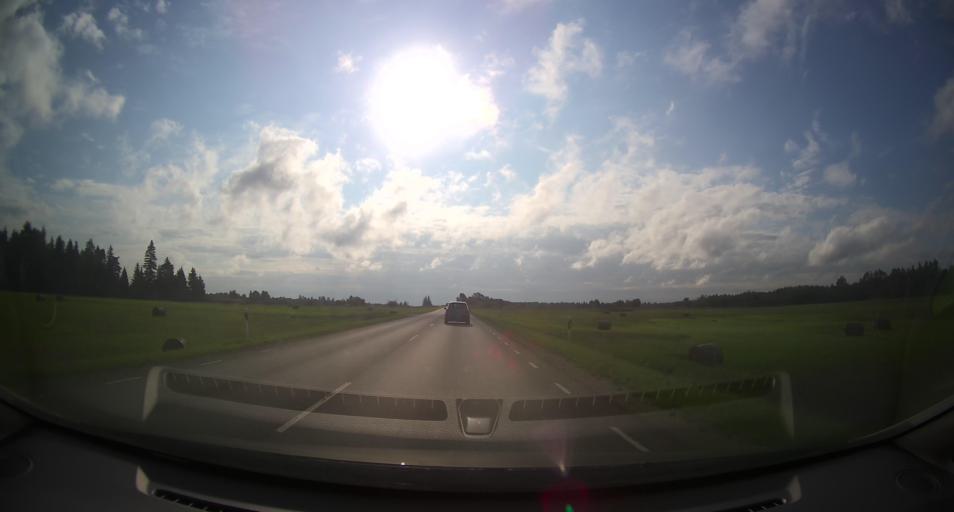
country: EE
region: Harju
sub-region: Raasiku vald
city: Raasiku
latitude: 59.4099
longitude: 25.2518
